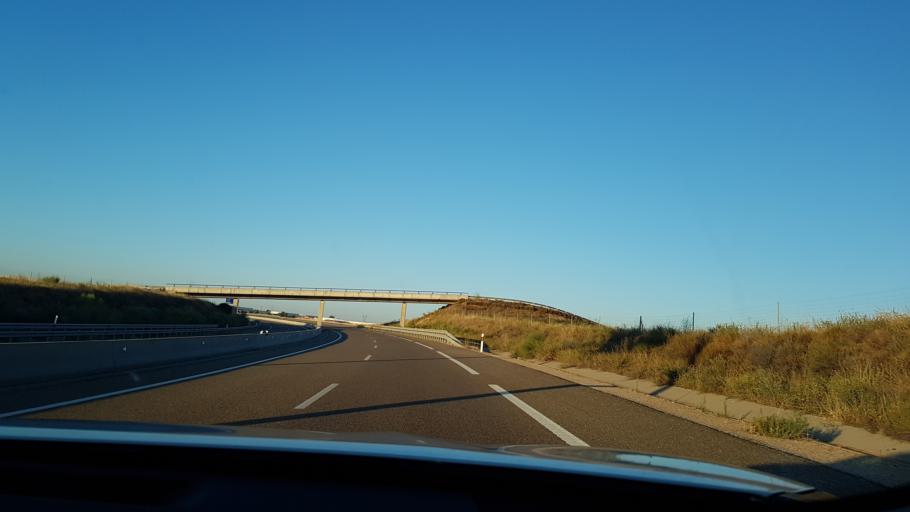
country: ES
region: Castille and Leon
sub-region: Provincia de Zamora
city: Valcabado
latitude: 41.5521
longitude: -5.7563
